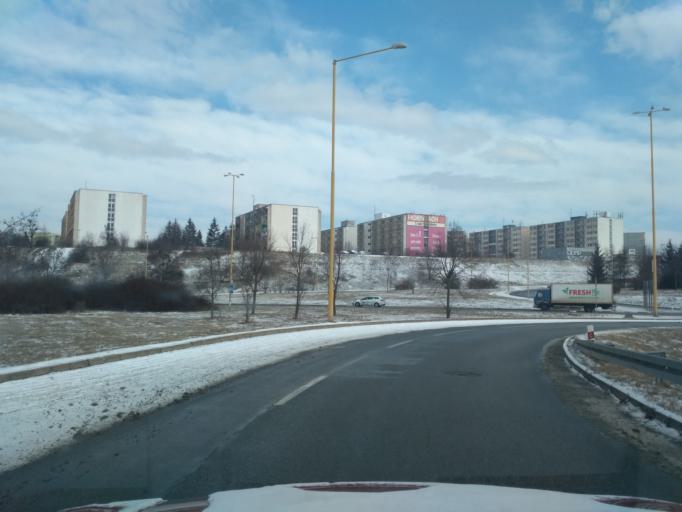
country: SK
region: Kosicky
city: Kosice
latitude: 48.6945
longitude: 21.2312
